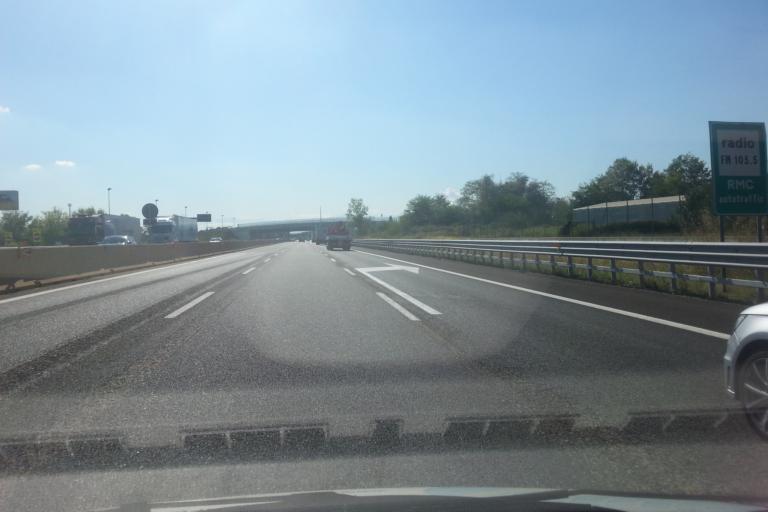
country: IT
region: Piedmont
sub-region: Provincia di Torino
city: Settimo Torinese
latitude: 45.1383
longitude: 7.7412
